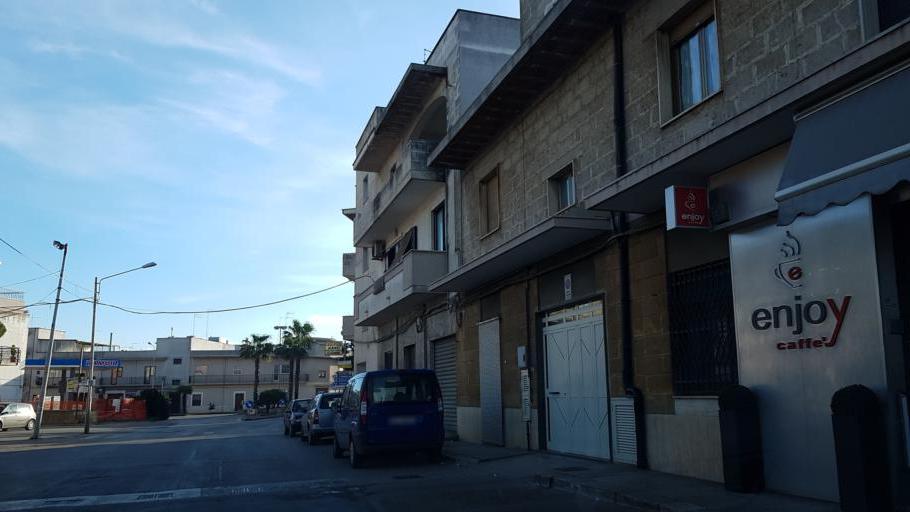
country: IT
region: Apulia
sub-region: Provincia di Brindisi
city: Carovigno
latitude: 40.7046
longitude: 17.6635
